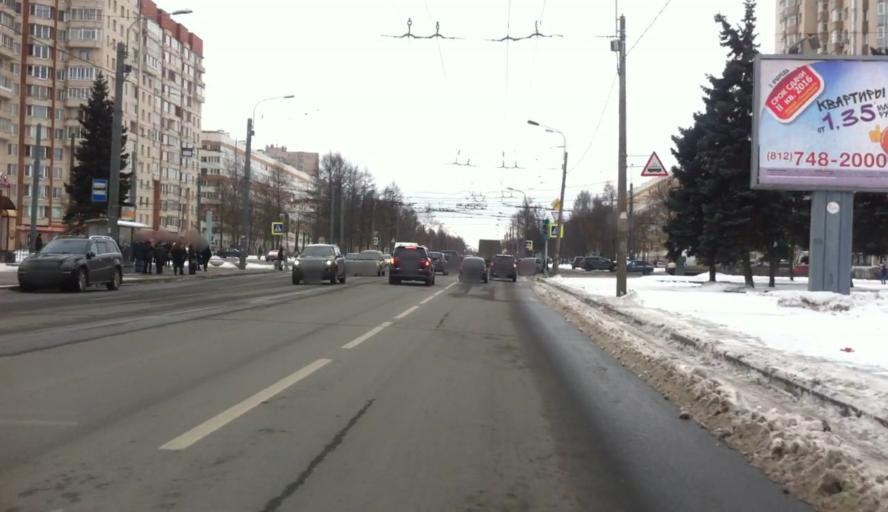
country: RU
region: St.-Petersburg
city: Uritsk
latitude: 59.8338
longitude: 30.1756
